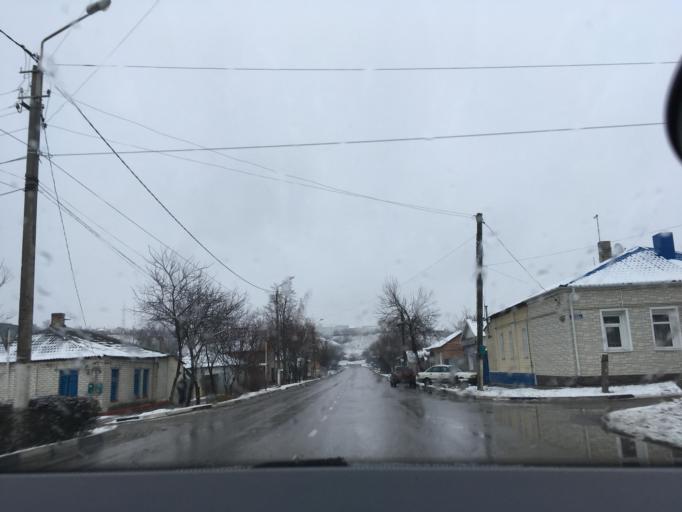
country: RU
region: Belgorod
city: Valuyki
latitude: 50.2080
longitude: 38.1082
